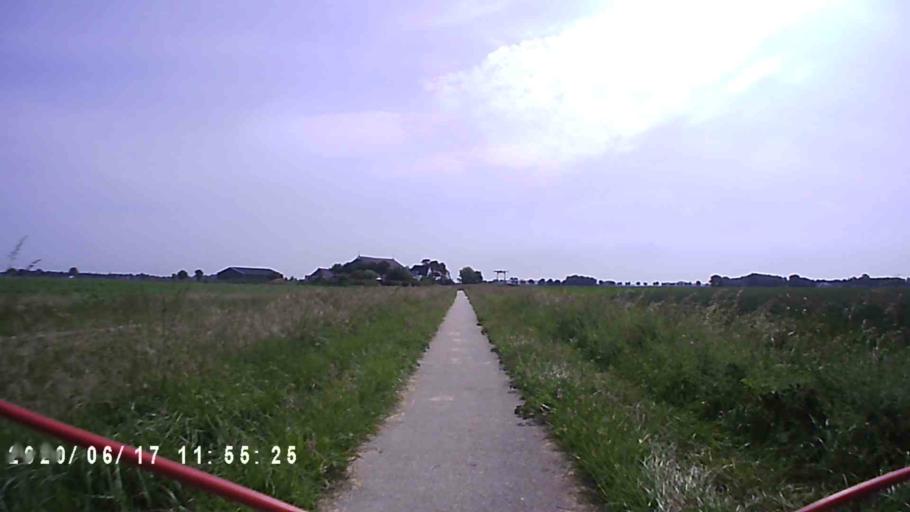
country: NL
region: Groningen
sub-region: Gemeente De Marne
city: Ulrum
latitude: 53.3490
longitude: 6.3164
